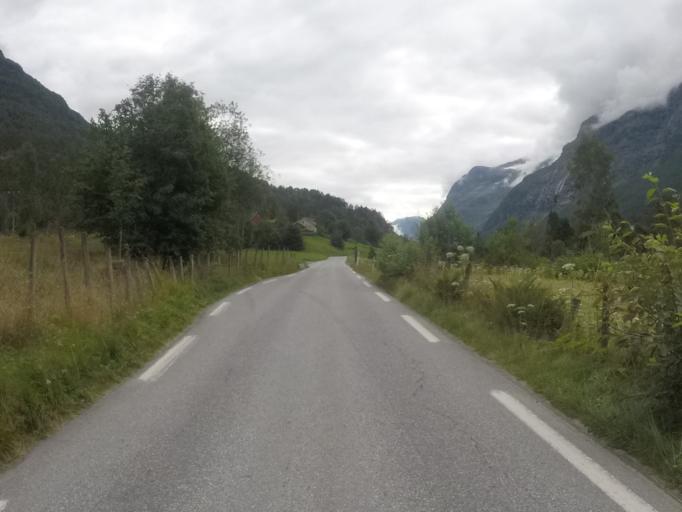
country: NO
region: Sogn og Fjordane
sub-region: Stryn
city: Stryn
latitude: 61.8662
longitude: 6.8827
